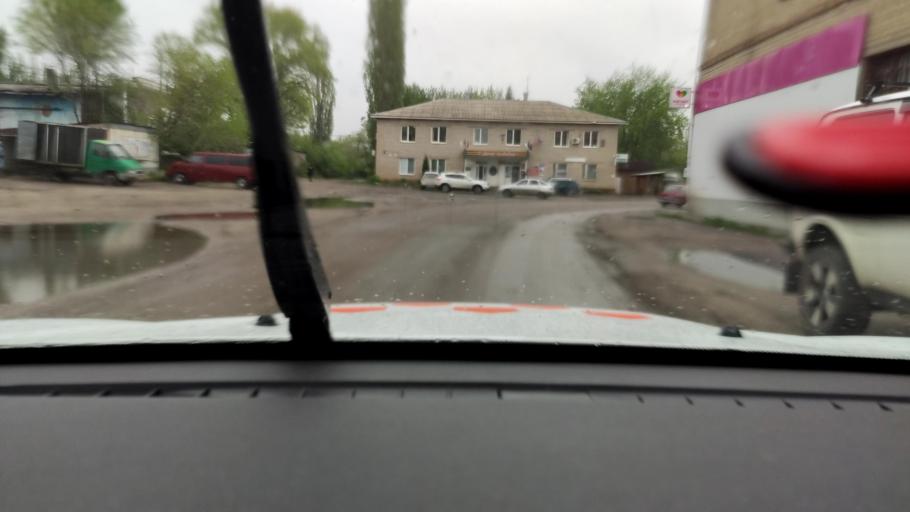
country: RU
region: Voronezj
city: Strelitsa
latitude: 51.6133
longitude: 38.8994
